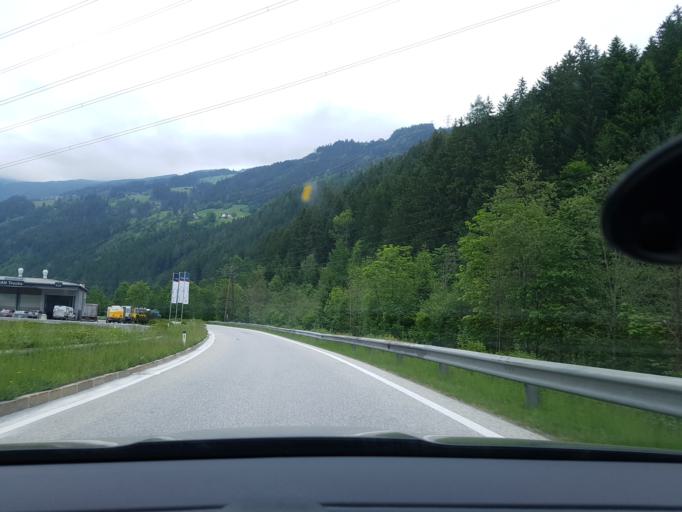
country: AT
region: Tyrol
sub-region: Politischer Bezirk Schwaz
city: Zell am Ziller
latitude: 47.2278
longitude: 11.8914
